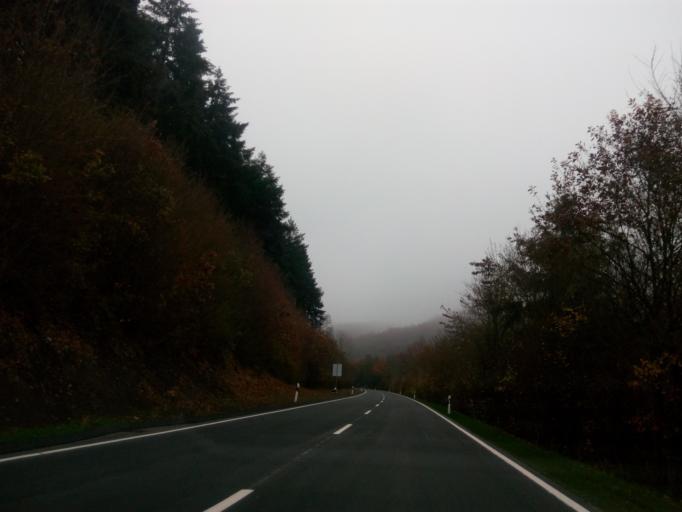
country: DE
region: Rheinland-Pfalz
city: Oberweiler-Tiefenbach
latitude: 49.6093
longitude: 7.6109
